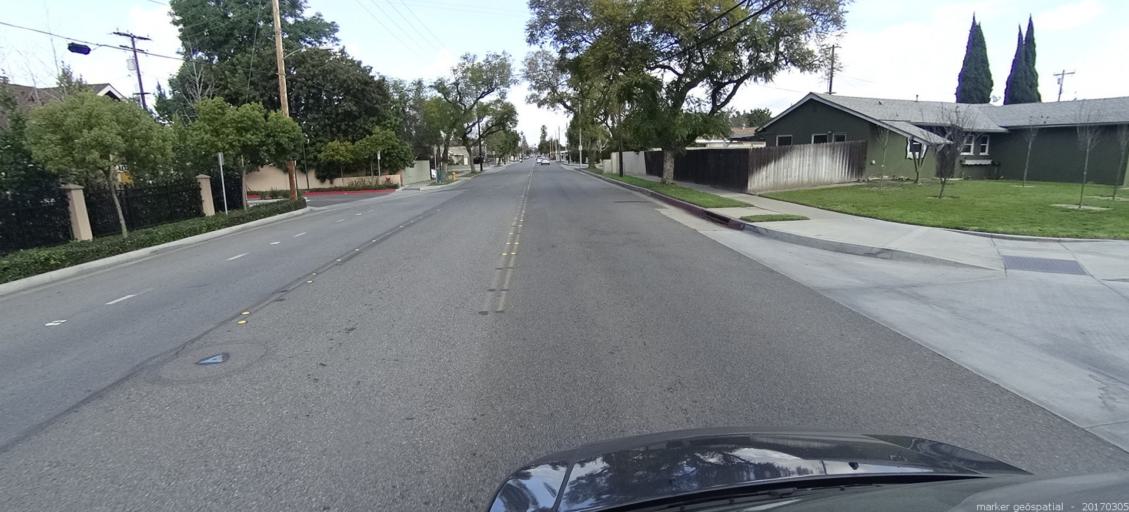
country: US
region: California
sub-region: Orange County
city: Anaheim
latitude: 33.8195
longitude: -117.9285
